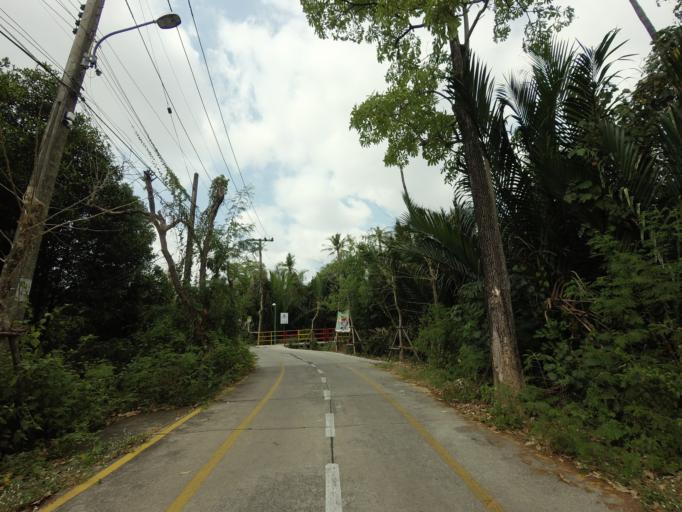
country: TH
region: Samut Prakan
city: Phra Pradaeng
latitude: 13.6624
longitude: 100.5652
